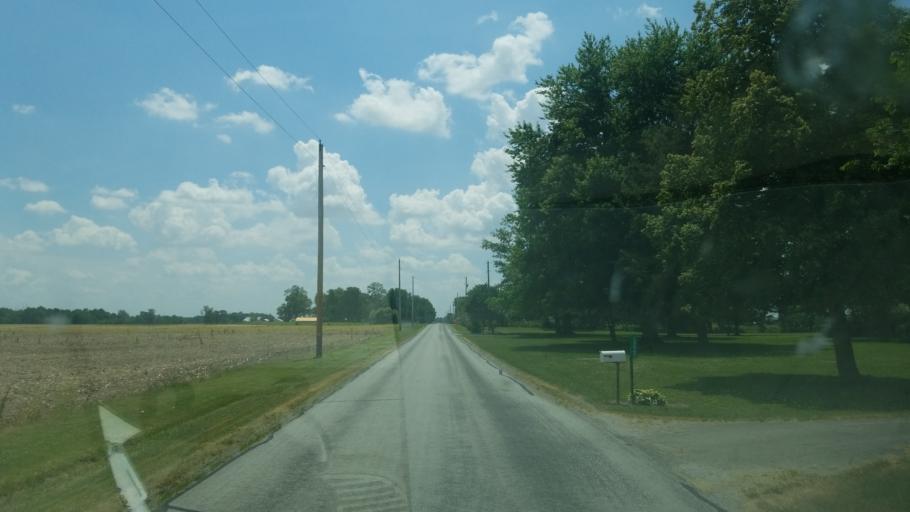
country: US
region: Ohio
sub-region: Hardin County
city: Kenton
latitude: 40.6236
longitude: -83.5603
